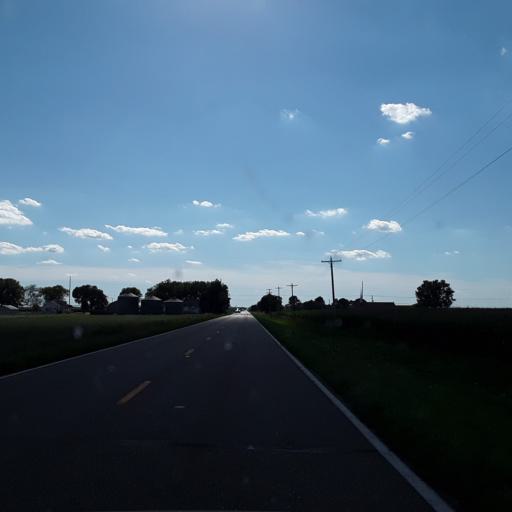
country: US
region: Nebraska
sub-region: Hall County
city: Wood River
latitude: 40.8878
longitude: -98.6221
